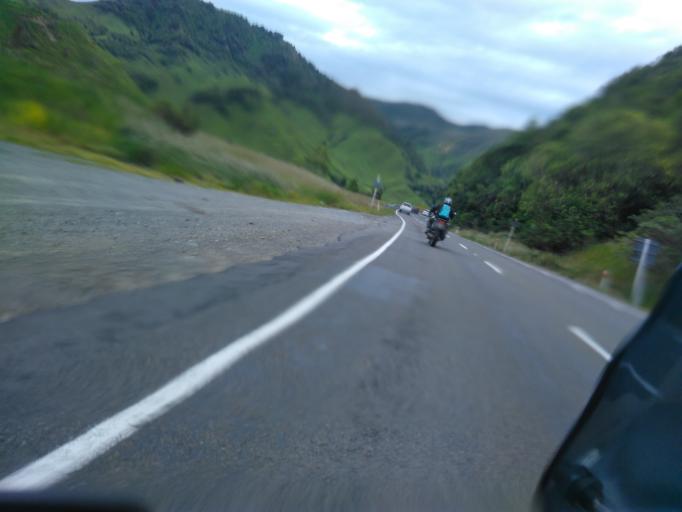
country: NZ
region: Bay of Plenty
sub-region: Opotiki District
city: Opotiki
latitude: -38.3613
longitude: 177.4547
